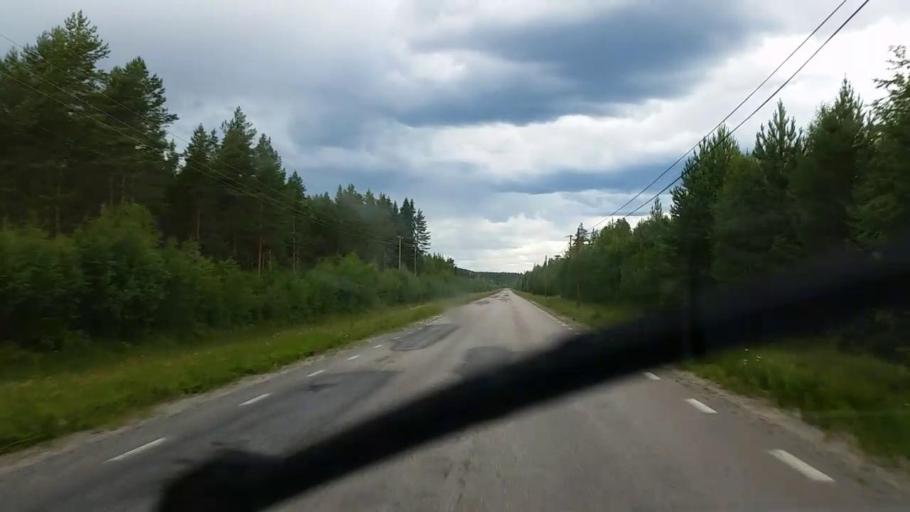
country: SE
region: Gaevleborg
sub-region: Ovanakers Kommun
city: Edsbyn
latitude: 61.4431
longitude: 15.8880
